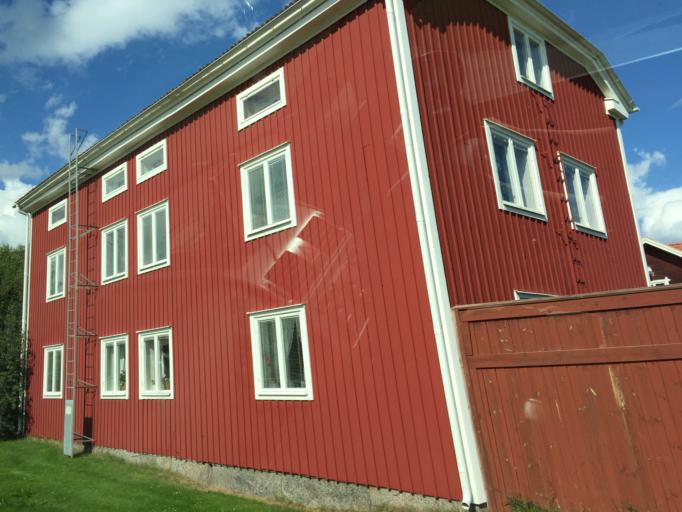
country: SE
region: Gaevleborg
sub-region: Bollnas Kommun
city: Arbra
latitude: 61.5003
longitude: 16.3595
